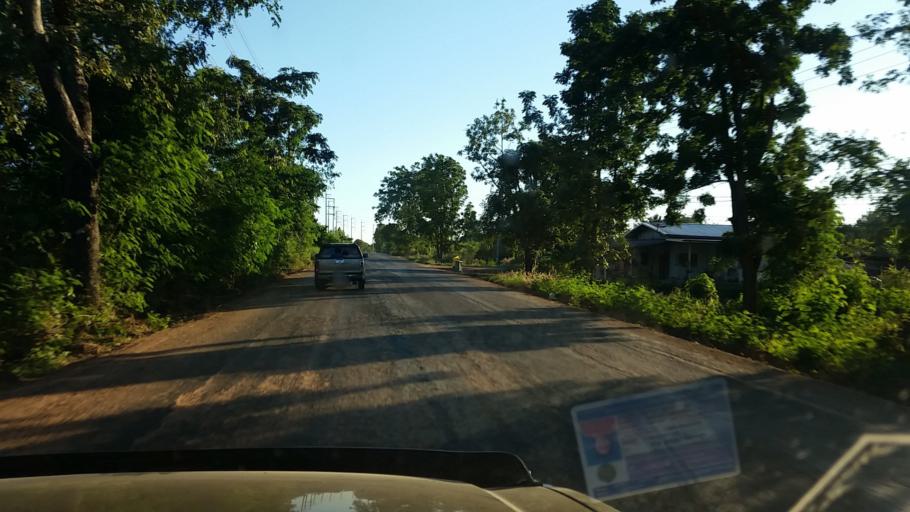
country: TH
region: Chaiyaphum
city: Nong Bua Rawe
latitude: 15.7468
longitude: 101.7576
